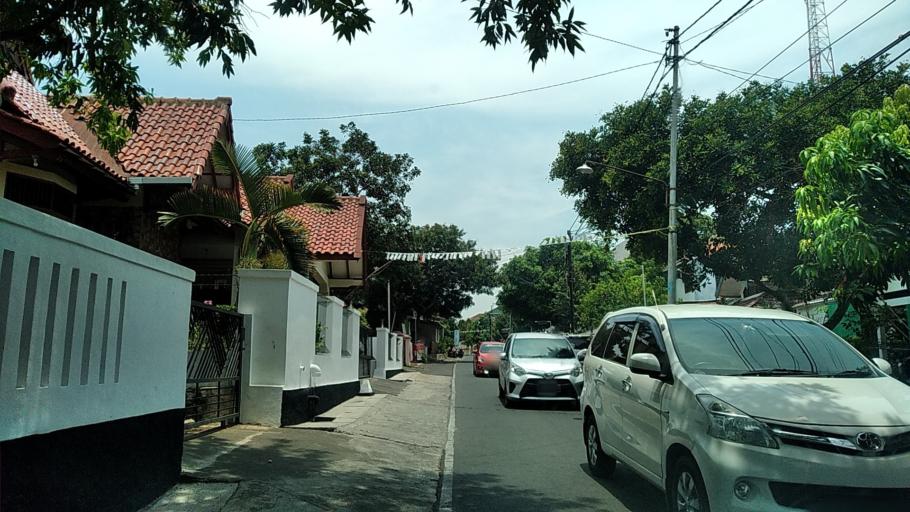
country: ID
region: Central Java
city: Semarang
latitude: -7.0597
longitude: 110.4122
